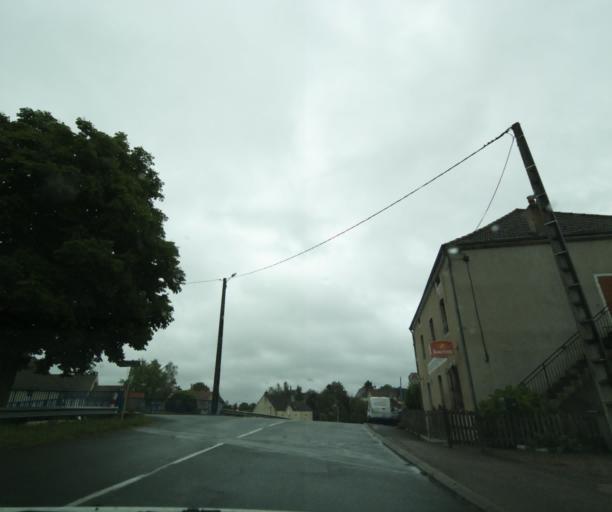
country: FR
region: Bourgogne
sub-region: Departement de Saone-et-Loire
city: Palinges
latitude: 46.5668
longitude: 4.2232
